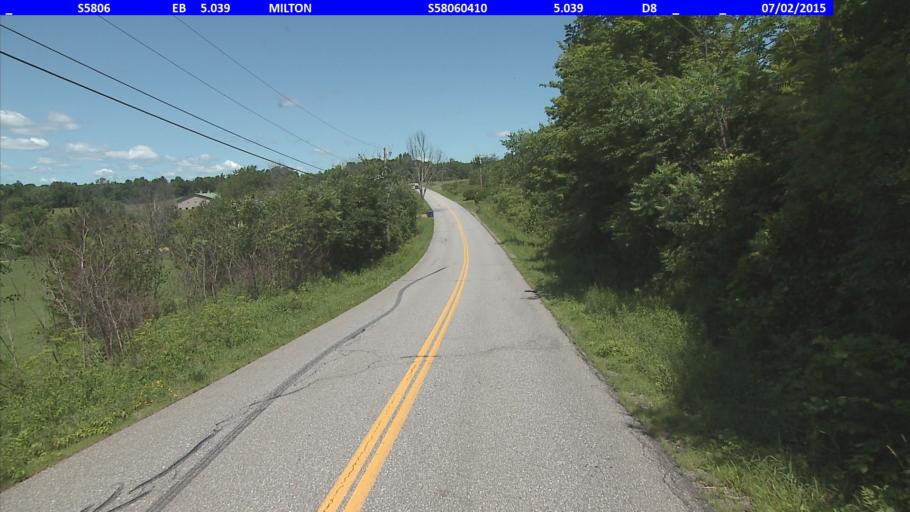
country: US
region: Vermont
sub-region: Chittenden County
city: Milton
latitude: 44.6932
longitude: -73.1786
